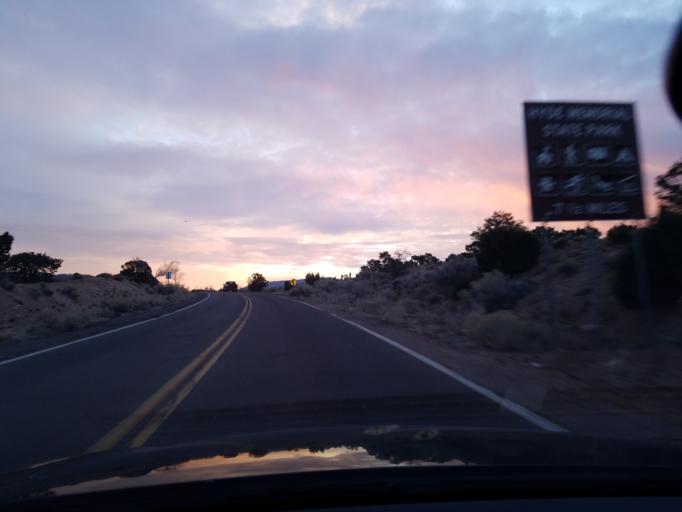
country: US
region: New Mexico
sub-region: Santa Fe County
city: Santa Fe
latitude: 35.6915
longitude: -105.9289
